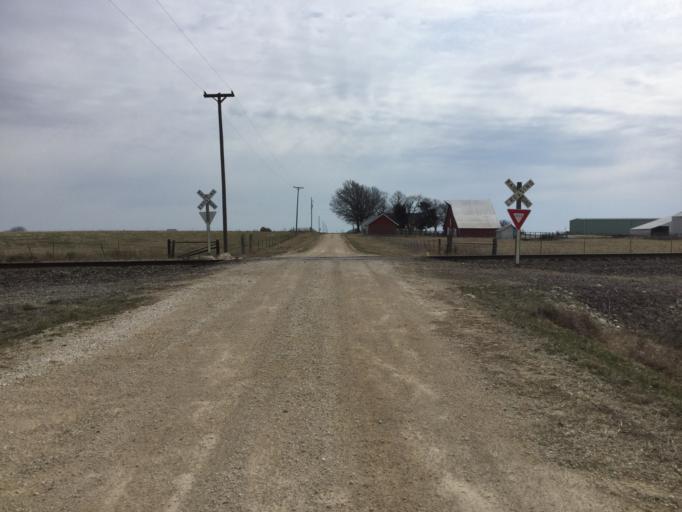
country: US
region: Kansas
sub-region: Allen County
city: Iola
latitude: 37.8634
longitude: -95.1613
